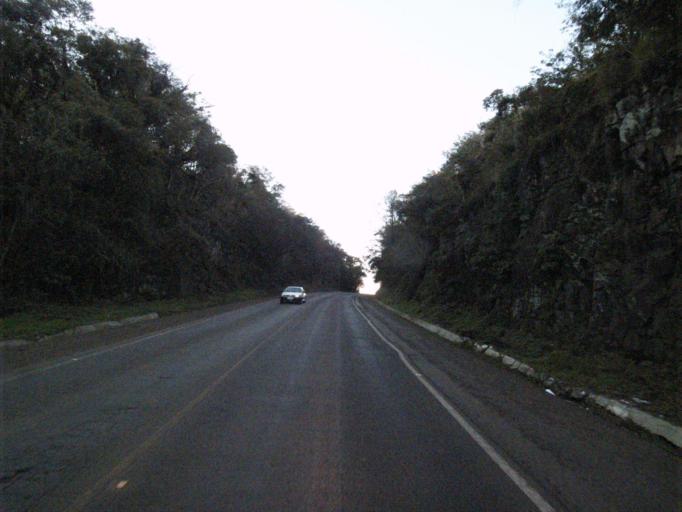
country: BR
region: Santa Catarina
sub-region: Sao Lourenco Do Oeste
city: Sao Lourenco dOeste
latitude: -26.7932
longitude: -53.1941
